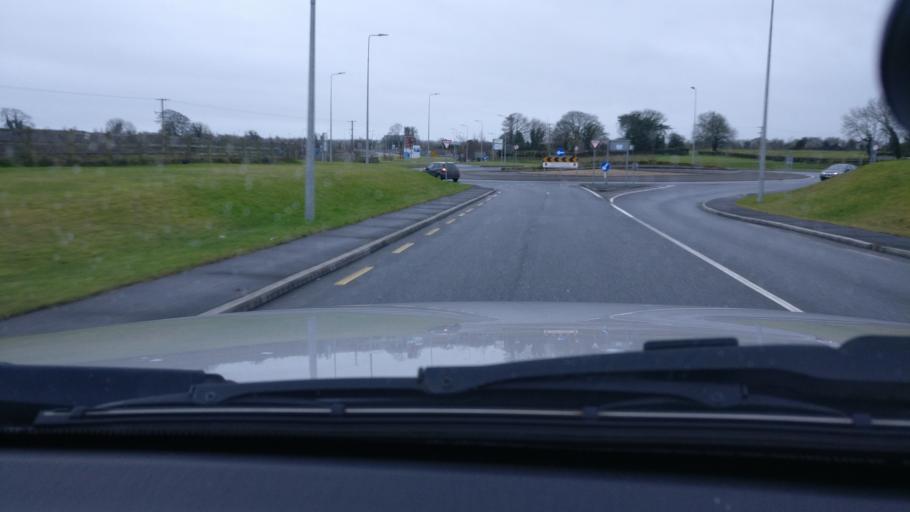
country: IE
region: Connaught
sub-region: County Galway
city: Ballinasloe
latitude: 53.3186
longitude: -8.2446
